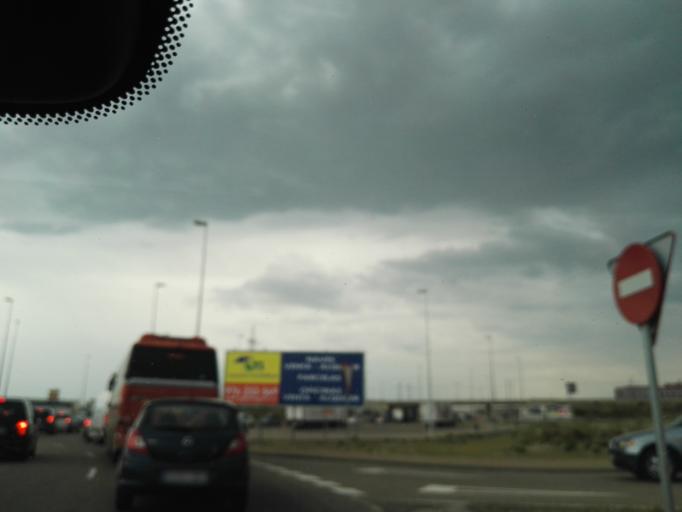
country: ES
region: Aragon
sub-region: Provincia de Zaragoza
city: Montecanal
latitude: 41.6390
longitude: -0.9927
